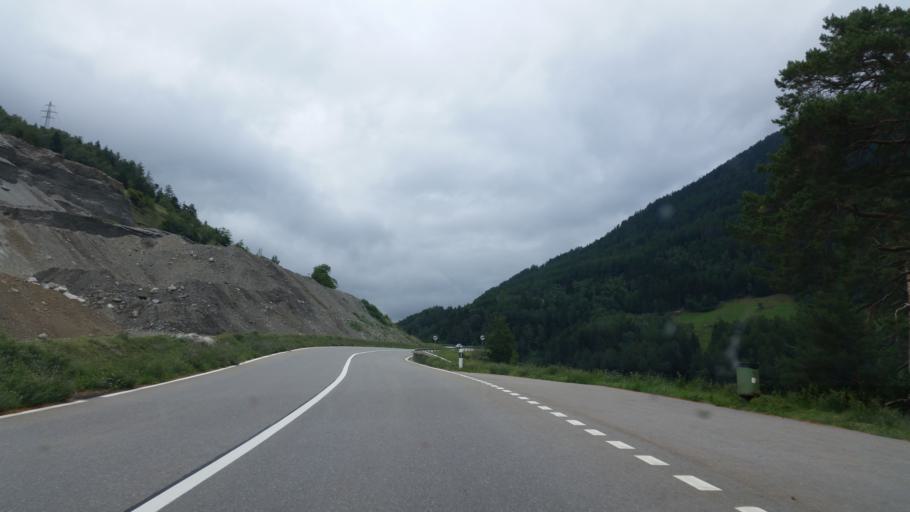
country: CH
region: Valais
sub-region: Entremont District
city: Orsieres
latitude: 46.0231
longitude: 7.1511
